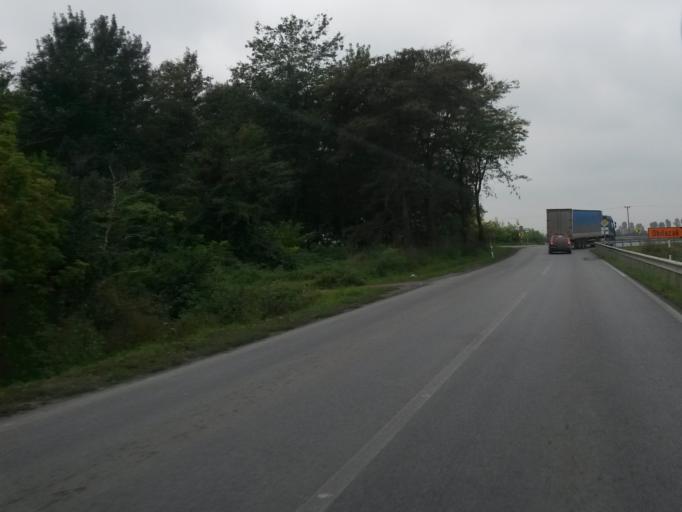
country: HR
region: Osjecko-Baranjska
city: Brijest
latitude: 45.5340
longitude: 18.6490
